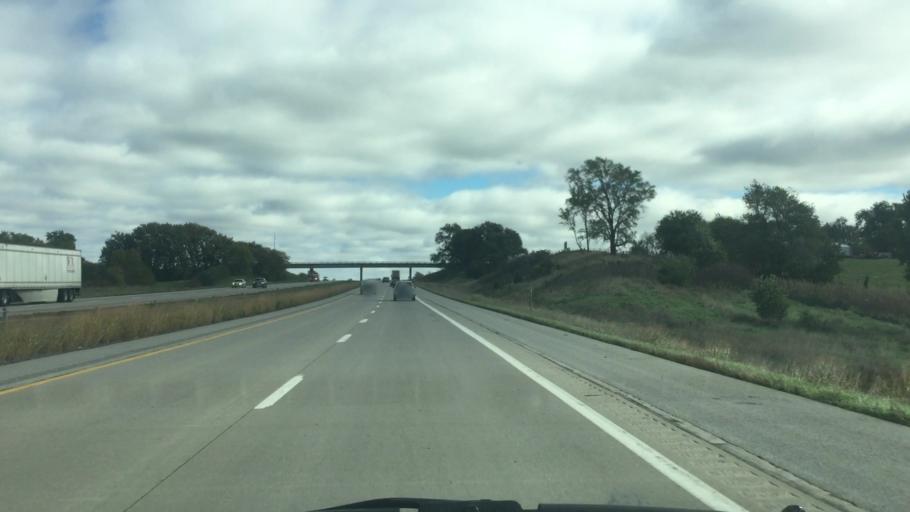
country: US
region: Iowa
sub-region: Jasper County
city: Newton
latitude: 41.6814
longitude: -93.1206
